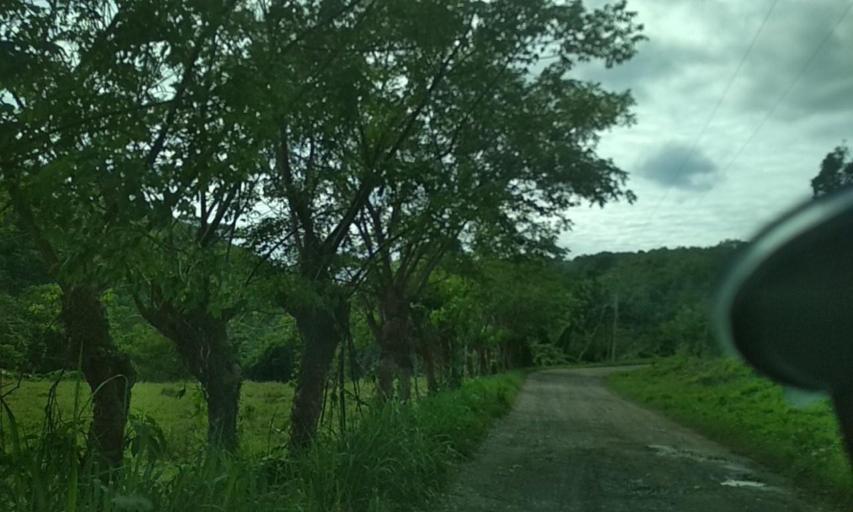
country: MX
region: Veracruz
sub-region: Papantla
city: Polutla
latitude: 20.5661
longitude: -97.1977
